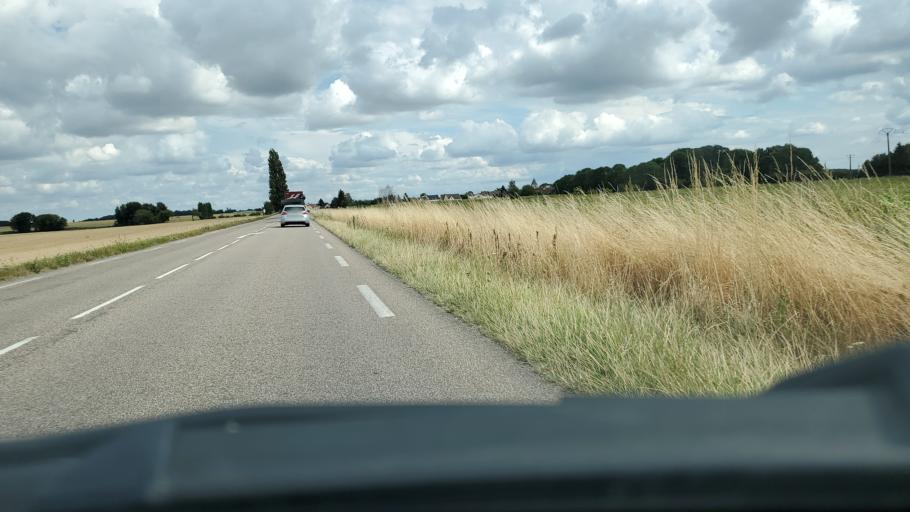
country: FR
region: Ile-de-France
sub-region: Departement de Seine-et-Marne
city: La Chapelle-sur-Crecy
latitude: 48.8904
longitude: 2.9497
